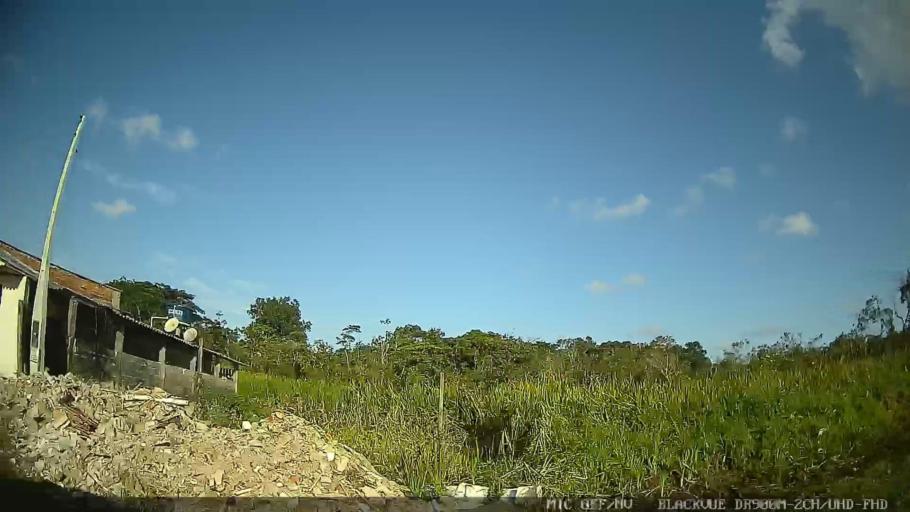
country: BR
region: Sao Paulo
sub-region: Itanhaem
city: Itanhaem
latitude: -24.1594
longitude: -46.8304
